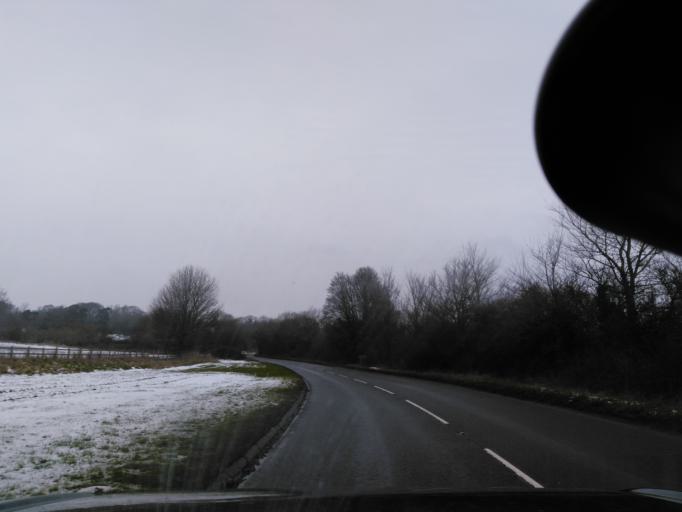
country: GB
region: England
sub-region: Wiltshire
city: Chippenham
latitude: 51.4406
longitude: -2.1321
